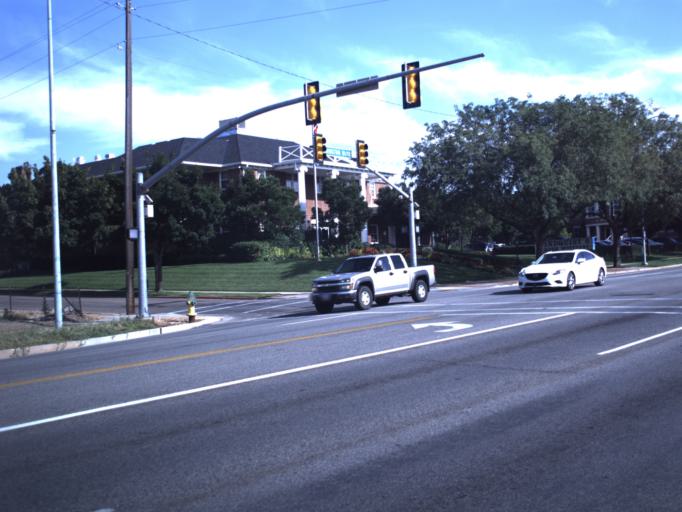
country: US
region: Utah
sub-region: Weber County
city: South Ogden
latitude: 41.2022
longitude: -111.9710
